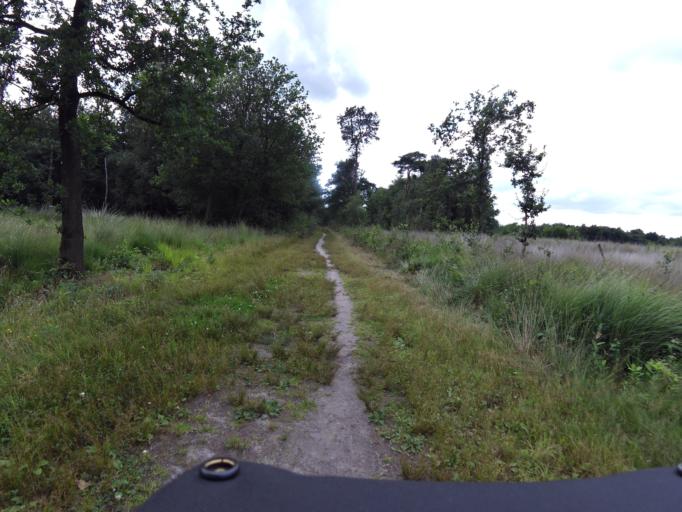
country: BE
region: Flanders
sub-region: Provincie Antwerpen
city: Baarle-Hertog
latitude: 51.4143
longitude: 4.8367
